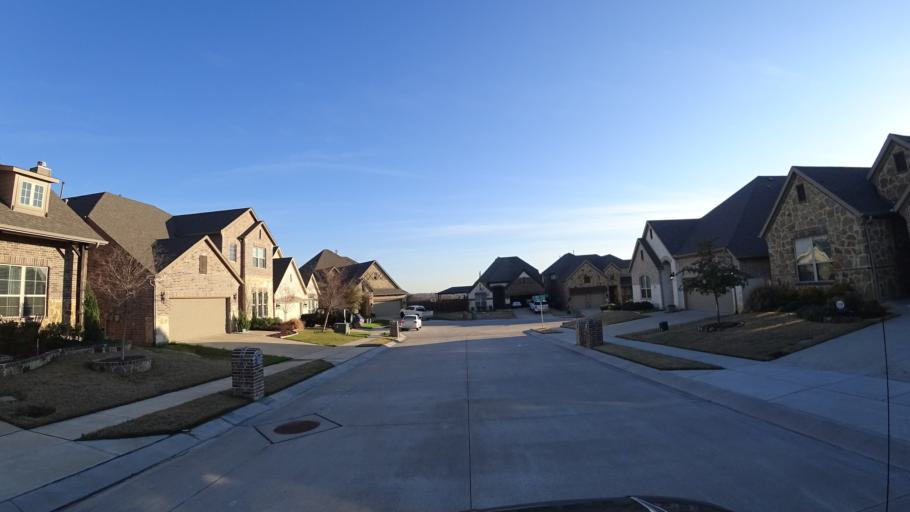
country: US
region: Texas
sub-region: Dallas County
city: Coppell
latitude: 32.9942
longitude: -96.9947
